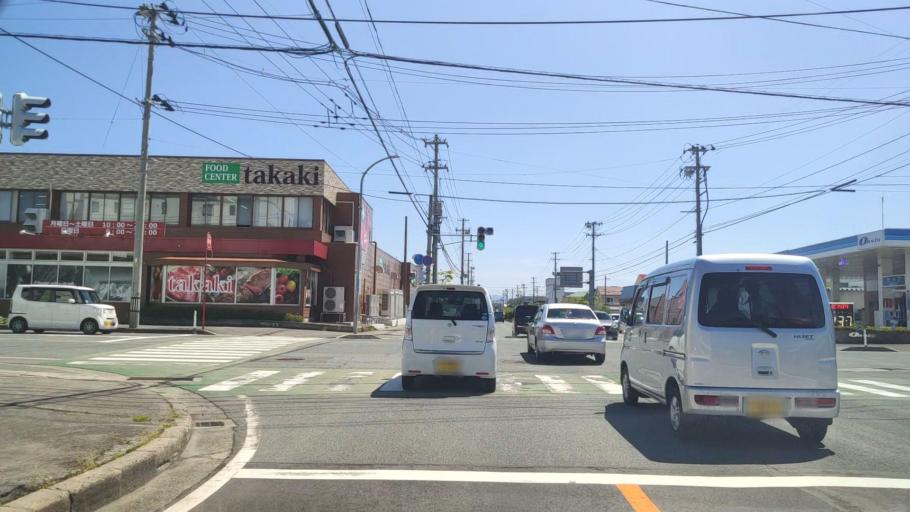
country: JP
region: Yamagata
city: Tendo
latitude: 38.3662
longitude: 140.3673
